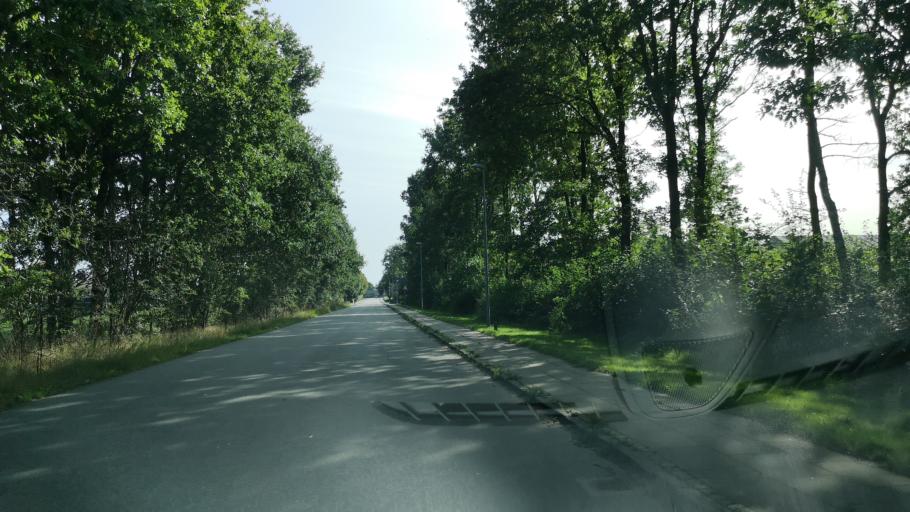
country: DK
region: Central Jutland
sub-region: Ikast-Brande Kommune
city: Ikast
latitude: 56.1492
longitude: 9.1388
